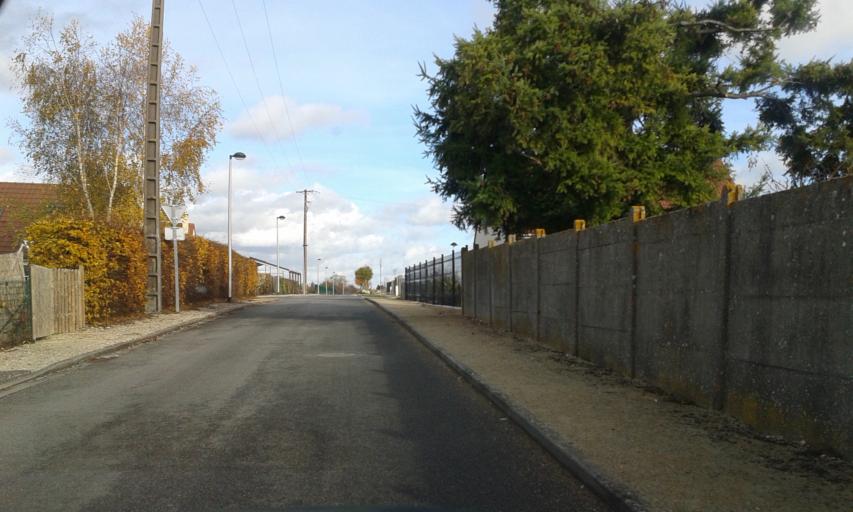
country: FR
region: Centre
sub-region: Departement du Loiret
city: Tavers
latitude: 47.7610
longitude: 1.6123
